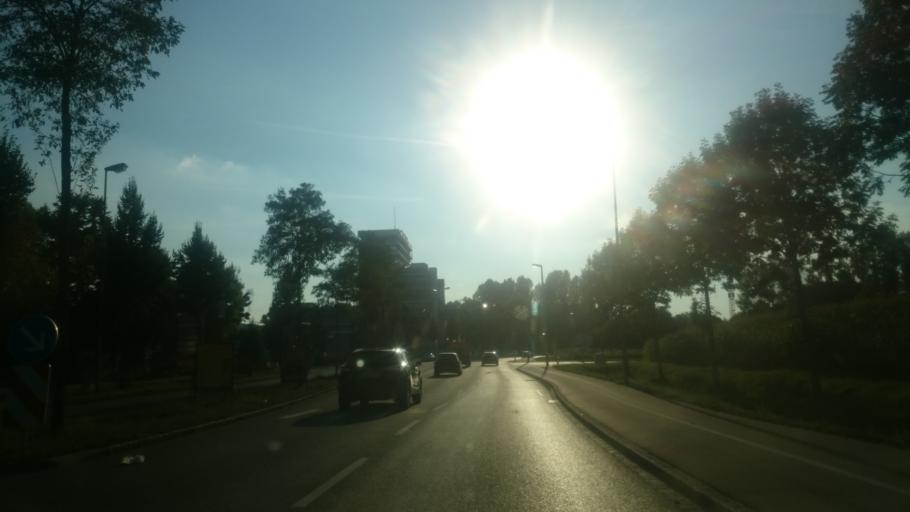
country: DE
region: Bavaria
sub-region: Swabia
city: Augsburg
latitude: 48.3971
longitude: 10.9241
